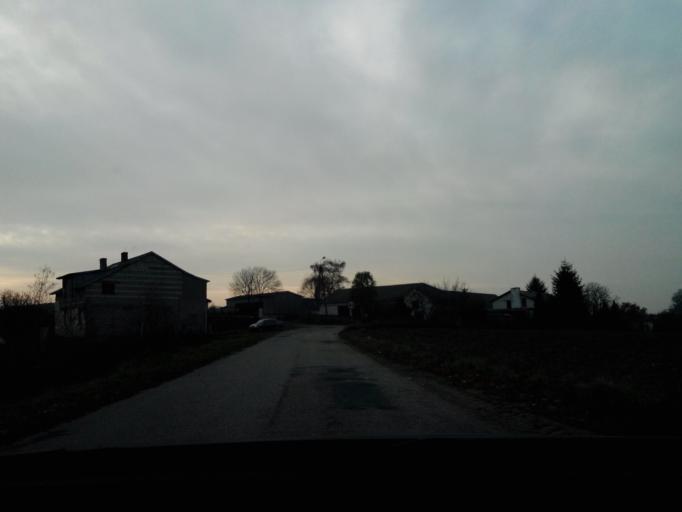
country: PL
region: Kujawsko-Pomorskie
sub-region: Powiat brodnicki
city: Swiedziebnia
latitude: 53.2151
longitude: 19.5241
